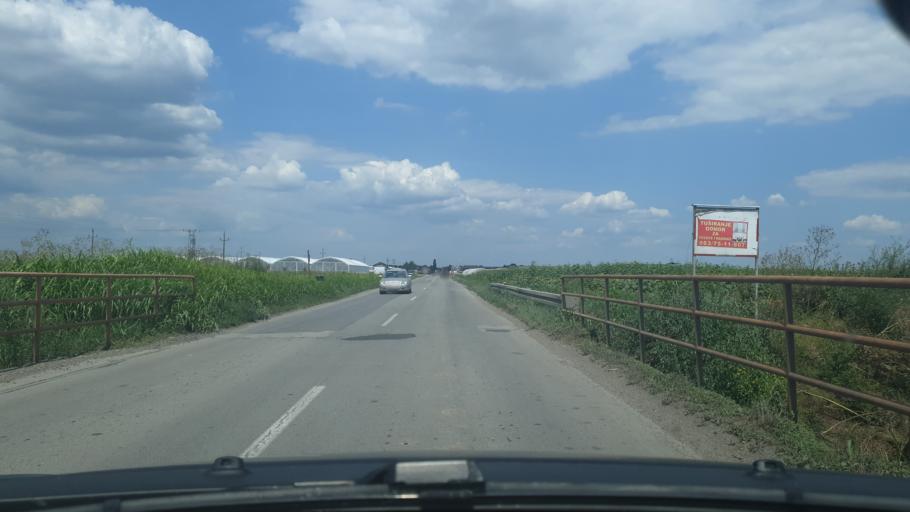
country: RS
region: Autonomna Pokrajina Vojvodina
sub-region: Sremski Okrug
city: Pecinci
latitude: 44.8879
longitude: 19.9626
